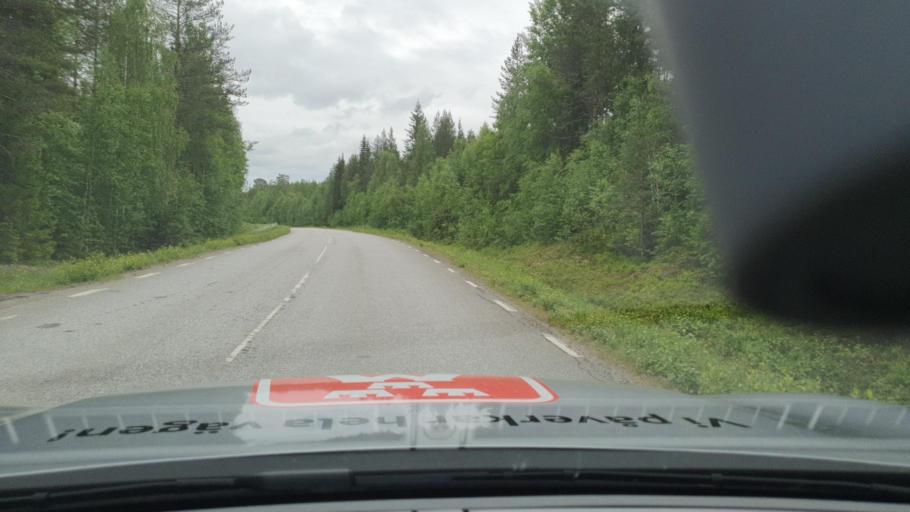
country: SE
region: Norrbotten
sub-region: Lulea Kommun
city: Ranea
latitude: 65.8871
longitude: 22.1950
